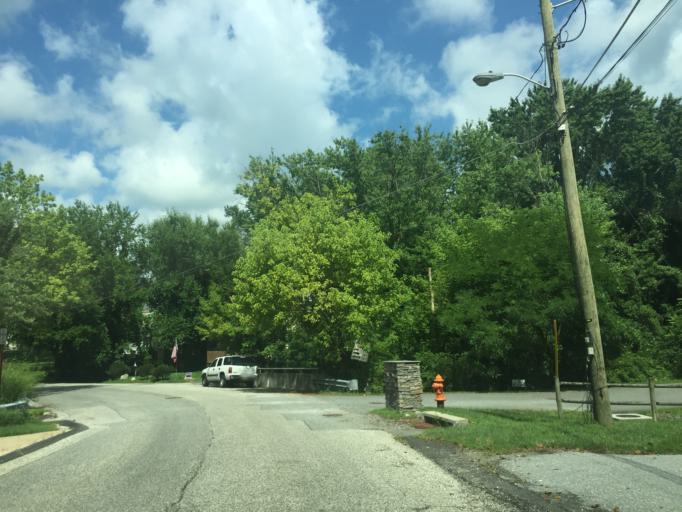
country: US
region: Maryland
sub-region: Baltimore County
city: Carney
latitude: 39.4021
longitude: -76.5128
